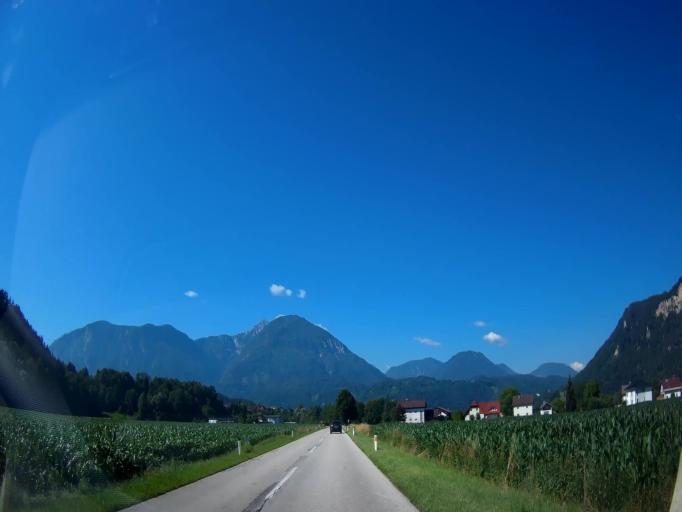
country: AT
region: Carinthia
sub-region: Politischer Bezirk Volkermarkt
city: Gallizien
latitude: 46.5823
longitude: 14.5122
